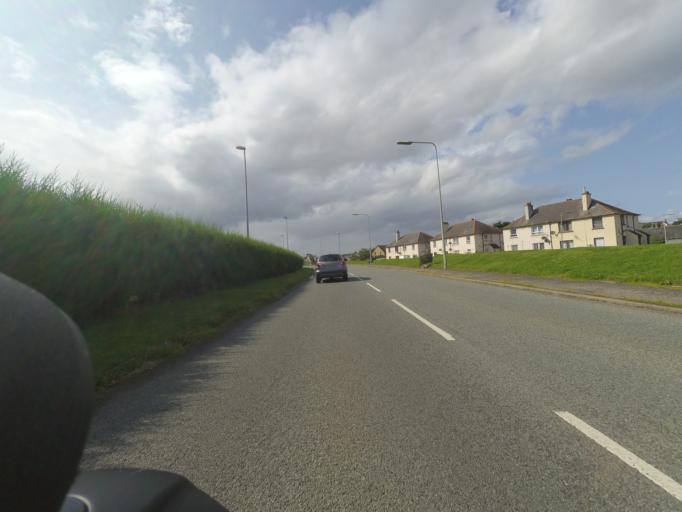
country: GB
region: Scotland
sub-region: Highland
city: Invergordon
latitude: 57.6867
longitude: -4.1712
